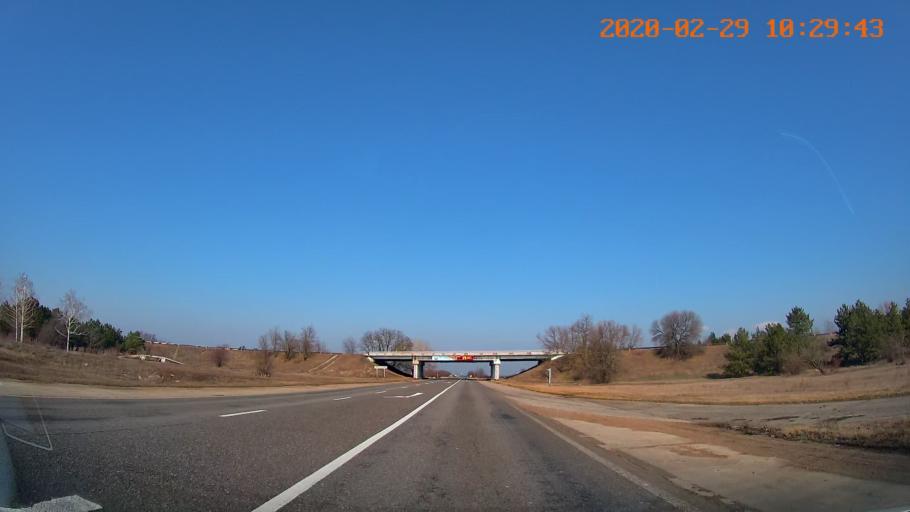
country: MD
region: Telenesti
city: Tiraspolul Nou
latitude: 46.9266
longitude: 29.5831
